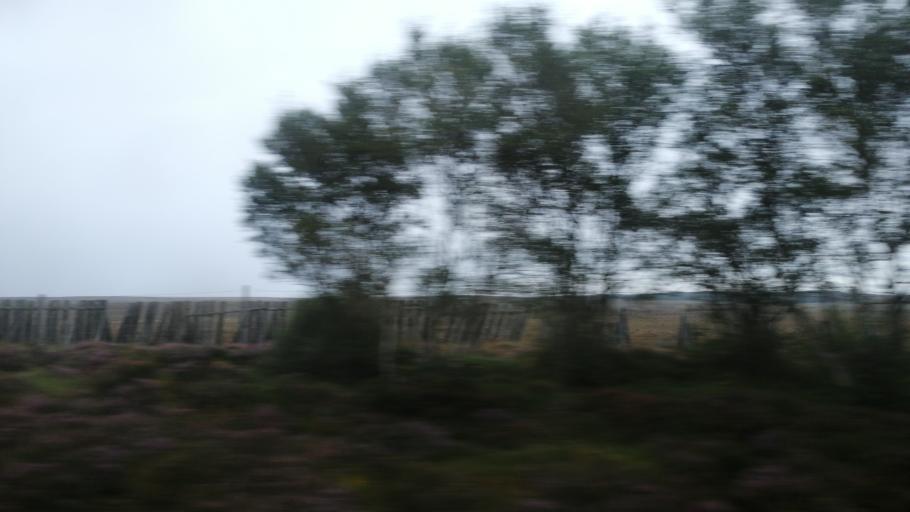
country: GB
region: Scotland
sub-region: Highland
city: Thurso
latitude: 58.3713
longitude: -3.7407
